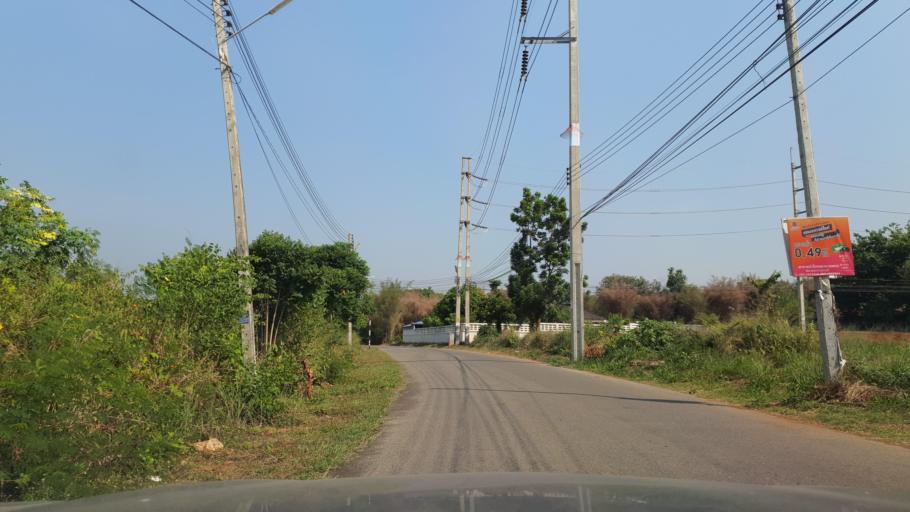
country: TH
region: Kanchanaburi
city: Kanchanaburi
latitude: 14.0681
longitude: 99.4859
